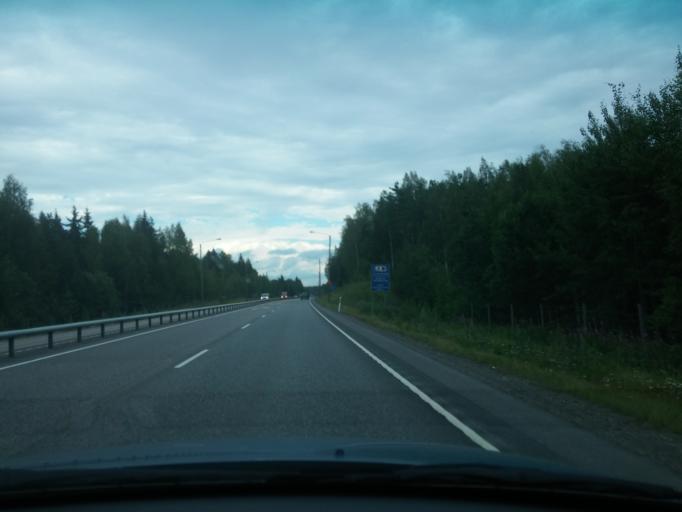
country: FI
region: Haeme
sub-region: Riihimaeki
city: Loppi
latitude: 60.7241
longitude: 24.5078
